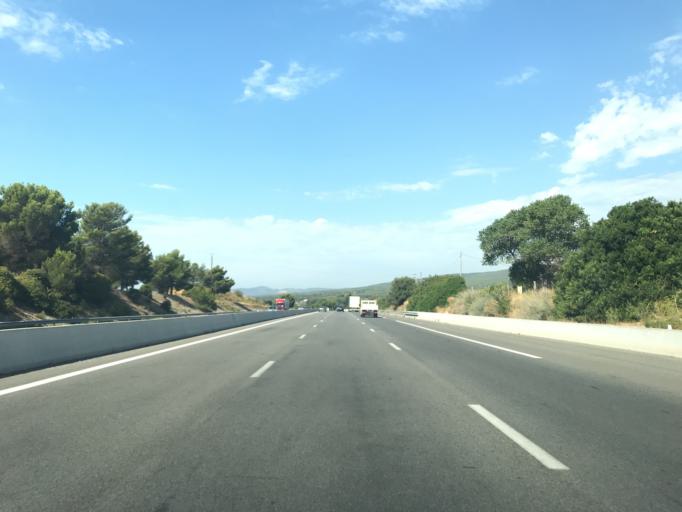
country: FR
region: Provence-Alpes-Cote d'Azur
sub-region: Departement du Var
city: Saint-Cyr-sur-Mer
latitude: 43.2029
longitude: 5.7376
